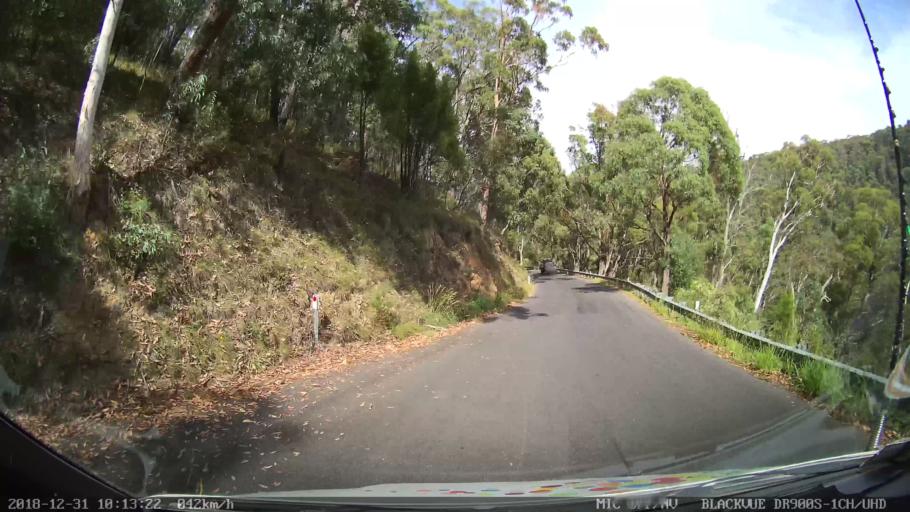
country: AU
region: New South Wales
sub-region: Snowy River
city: Jindabyne
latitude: -36.5379
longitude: 148.1554
